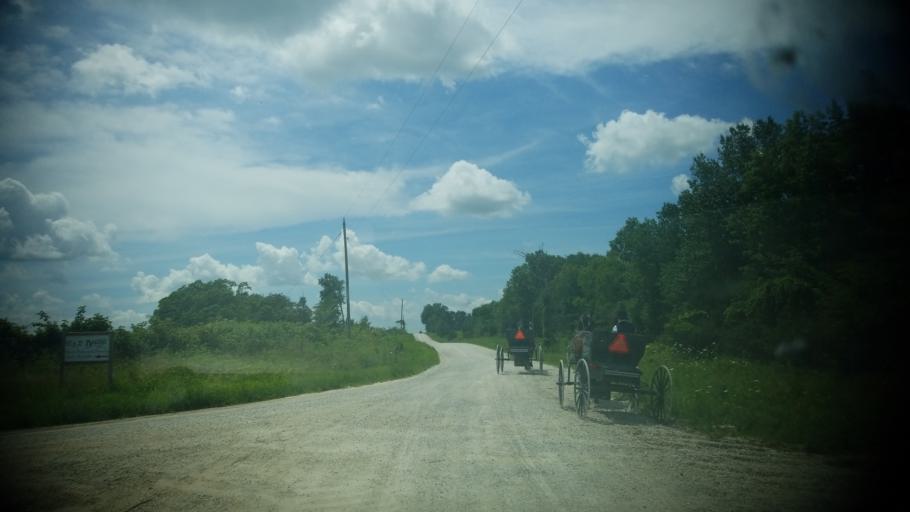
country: US
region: Missouri
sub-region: Pike County
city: Bowling Green
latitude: 39.3083
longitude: -91.3028
